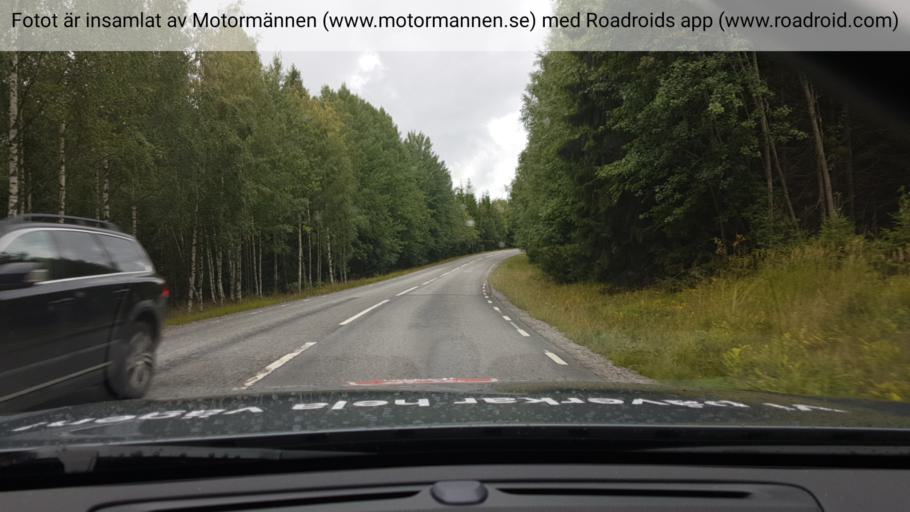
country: SE
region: Stockholm
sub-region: Botkyrka Kommun
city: Tullinge
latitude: 59.1455
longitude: 17.9337
